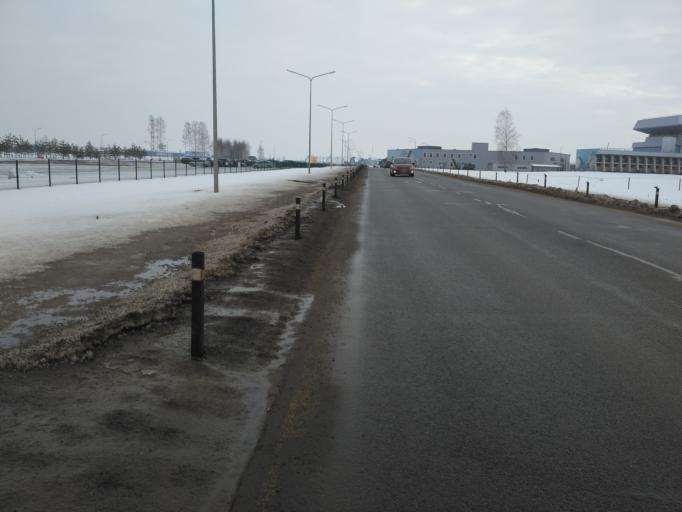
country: BY
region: Minsk
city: Horad Smalyavichy
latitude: 53.8928
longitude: 28.0342
